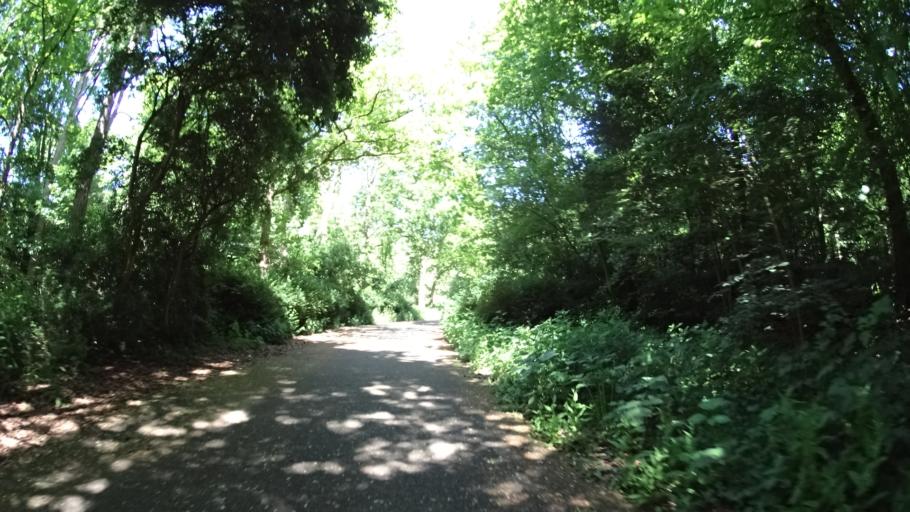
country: NL
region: South Holland
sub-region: Gemeente Den Haag
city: Scheveningen
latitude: 52.0959
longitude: 4.2906
